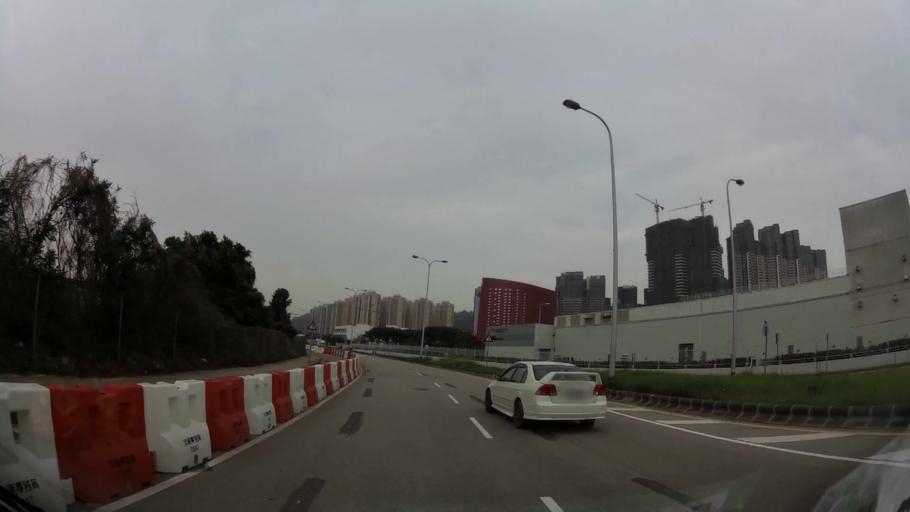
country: MO
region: Macau
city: Macau
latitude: 22.1321
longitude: 113.5540
